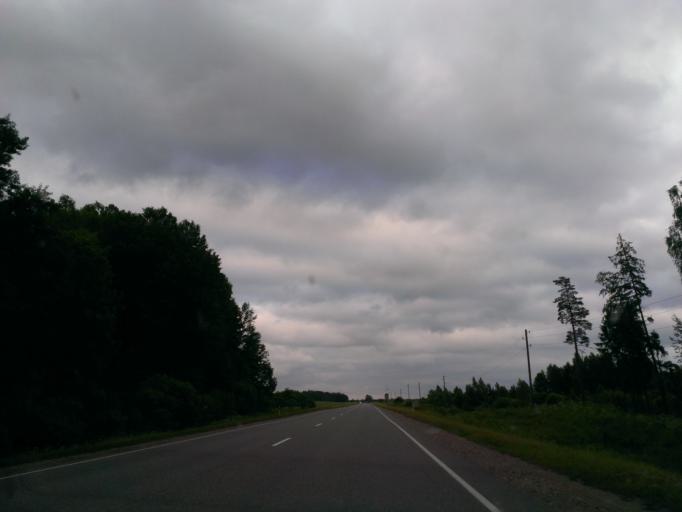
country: LV
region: Saldus Rajons
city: Saldus
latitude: 56.6715
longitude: 22.2853
